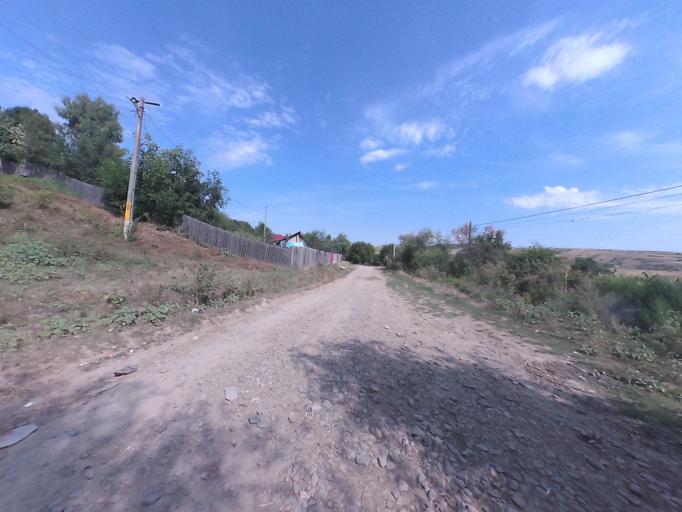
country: RO
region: Vaslui
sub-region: Comuna Osesti
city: Buda
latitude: 46.7620
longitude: 27.4093
